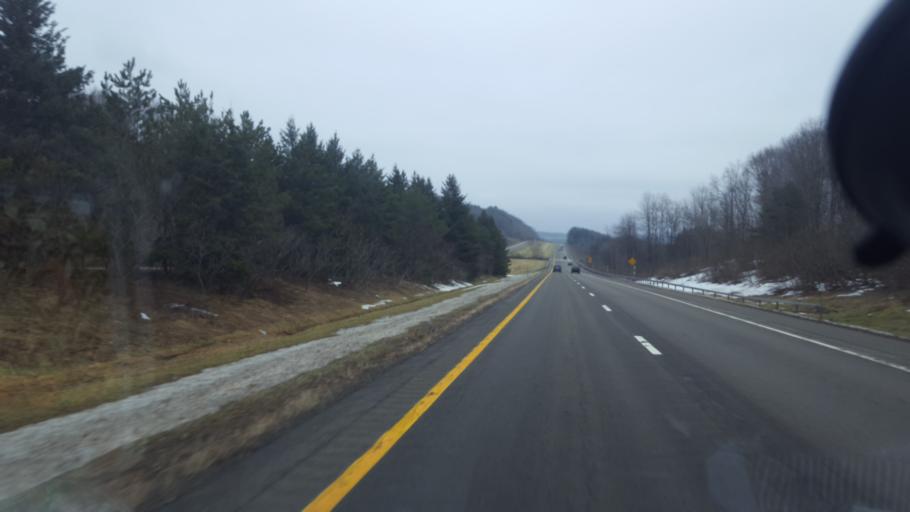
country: US
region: New York
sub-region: Chautauqua County
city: Falconer
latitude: 42.1352
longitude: -79.1312
